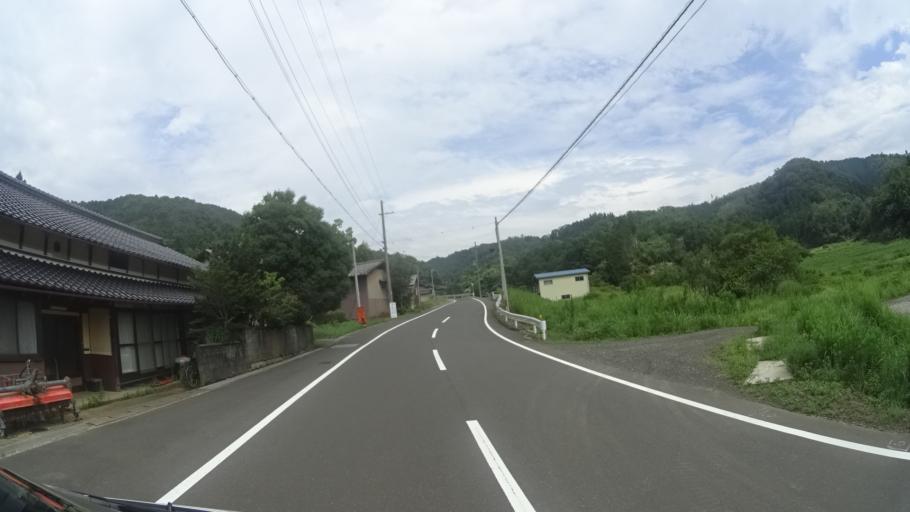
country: JP
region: Kyoto
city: Maizuru
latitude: 35.3560
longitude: 135.3328
